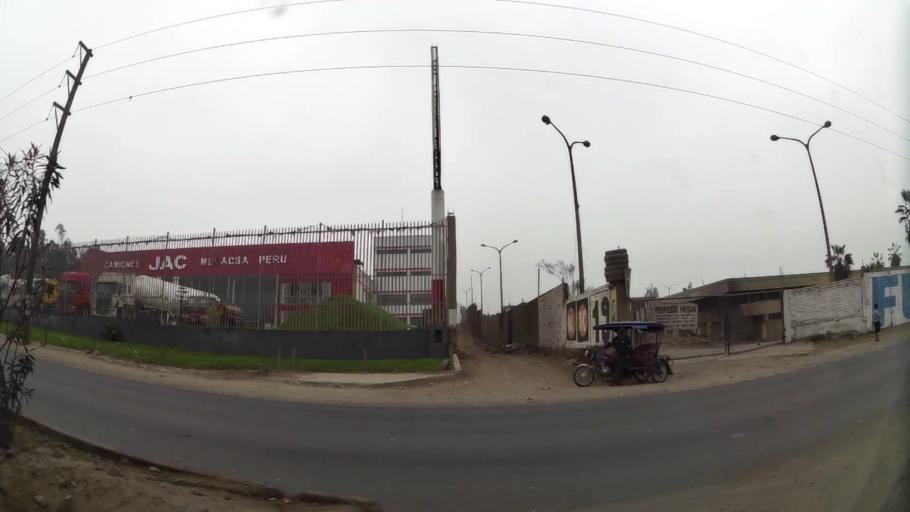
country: PE
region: Lima
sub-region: Lima
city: Santa Maria
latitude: -12.0210
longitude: -76.9045
